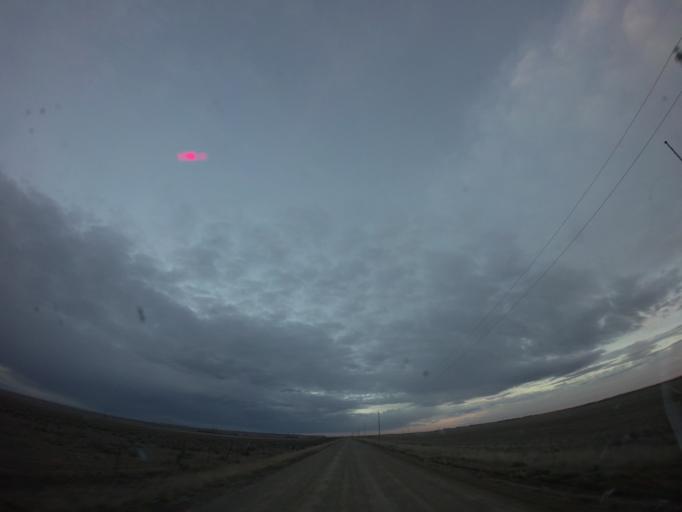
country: US
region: Montana
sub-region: Yellowstone County
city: Billings
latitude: 45.9436
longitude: -108.7264
